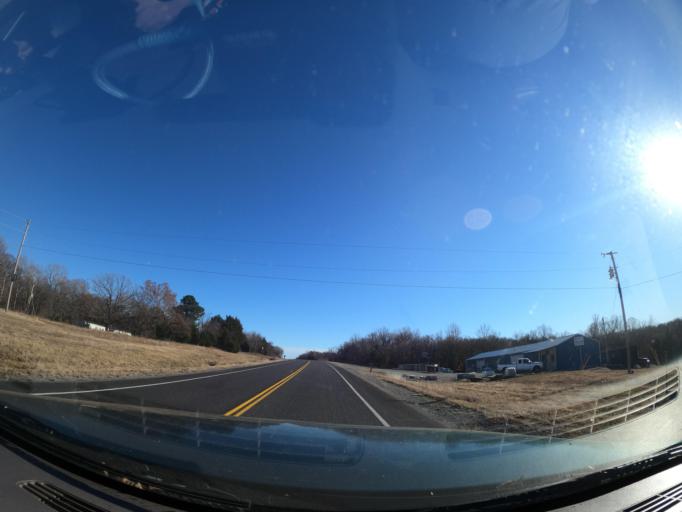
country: US
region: Oklahoma
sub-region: McIntosh County
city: Eufaula
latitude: 35.2542
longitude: -95.5756
